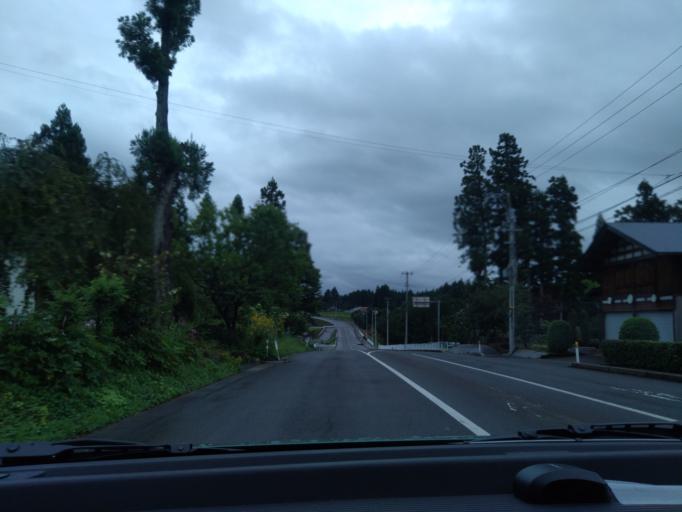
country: JP
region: Akita
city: Kakunodatemachi
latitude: 39.4623
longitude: 140.6219
